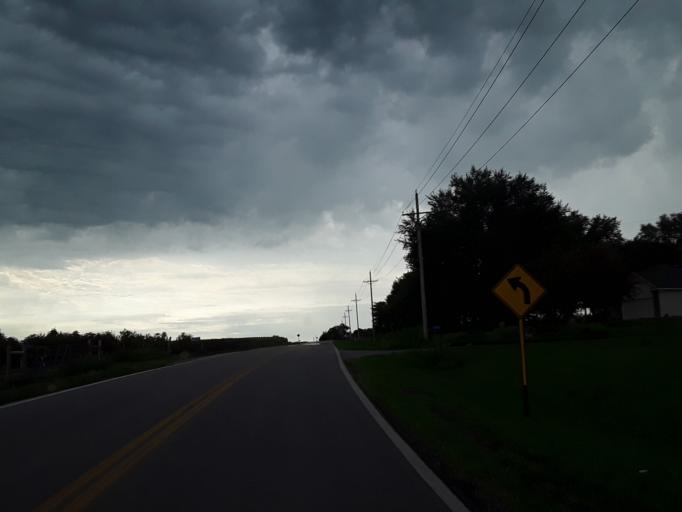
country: US
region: Nebraska
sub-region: Saunders County
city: Yutan
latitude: 41.1904
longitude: -96.3998
